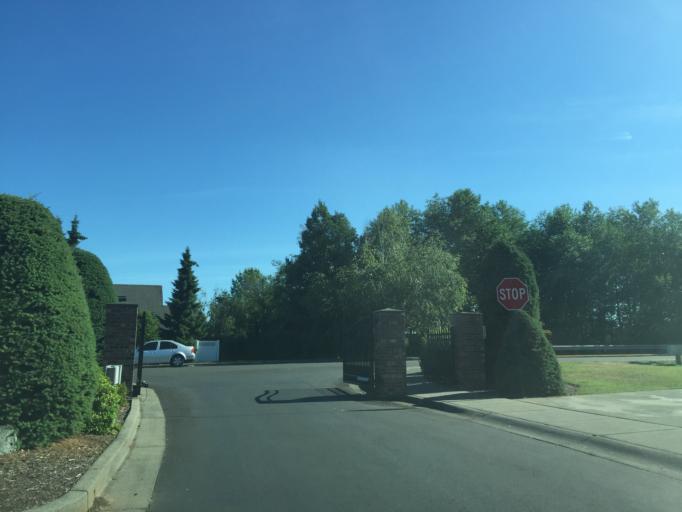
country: US
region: Washington
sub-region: Whatcom County
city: Lynden
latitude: 48.9627
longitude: -122.4333
